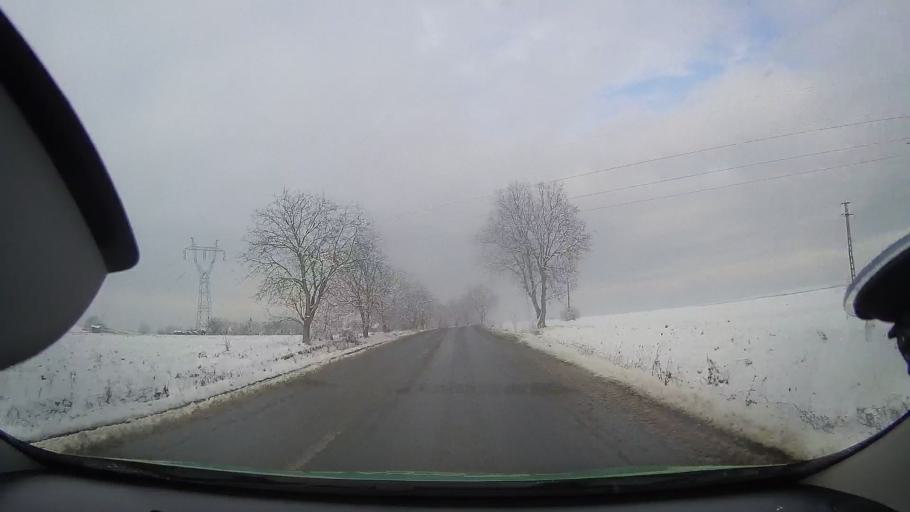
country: RO
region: Mures
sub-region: Comuna Atintis
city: Atintis
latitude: 46.4416
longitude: 24.0920
